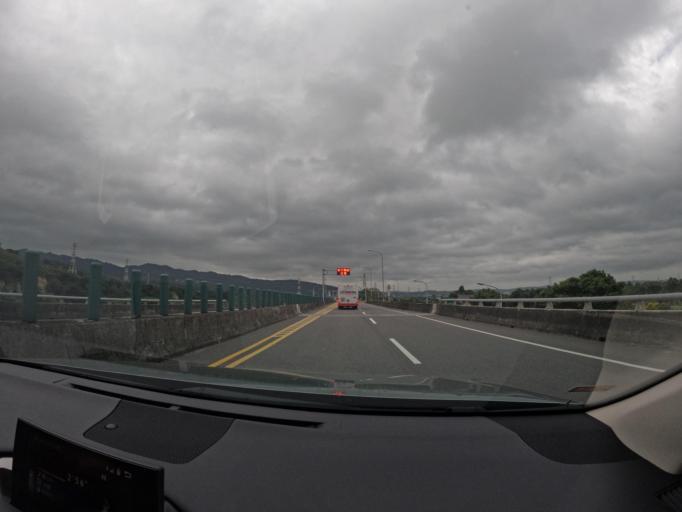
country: TW
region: Taiwan
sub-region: Miaoli
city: Miaoli
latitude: 24.4658
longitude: 120.8247
